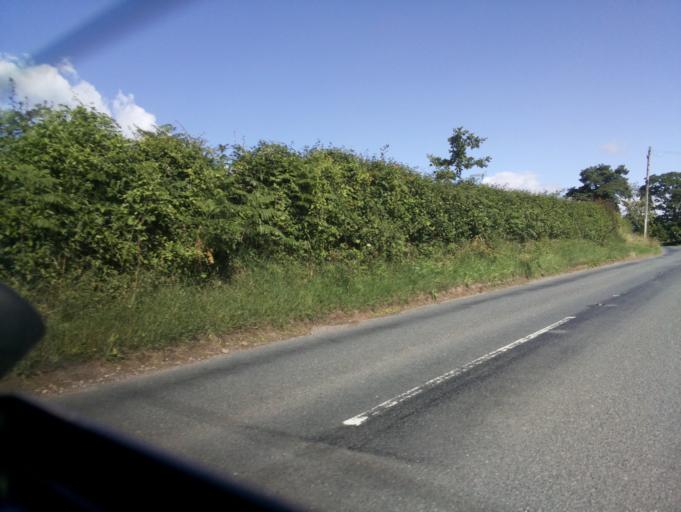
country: GB
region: England
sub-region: Herefordshire
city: Yatton
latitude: 51.9542
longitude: -2.5378
